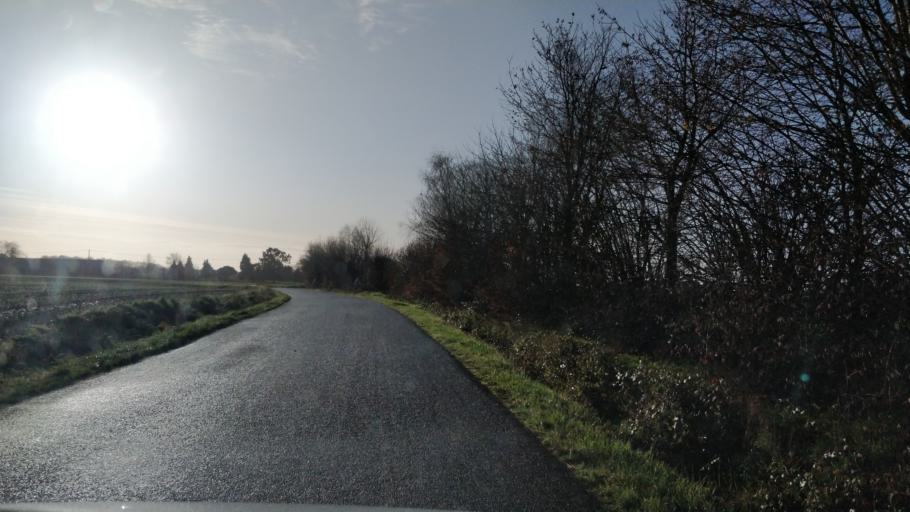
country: FR
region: Brittany
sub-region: Departement d'Ille-et-Vilaine
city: Chavagne
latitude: 48.0660
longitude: -1.7916
